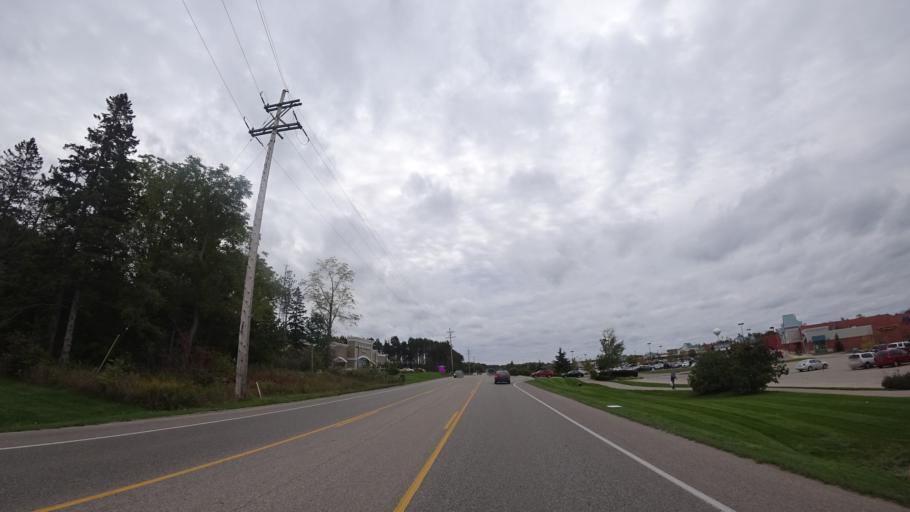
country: US
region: Michigan
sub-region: Emmet County
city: Petoskey
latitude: 45.3550
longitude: -84.9709
